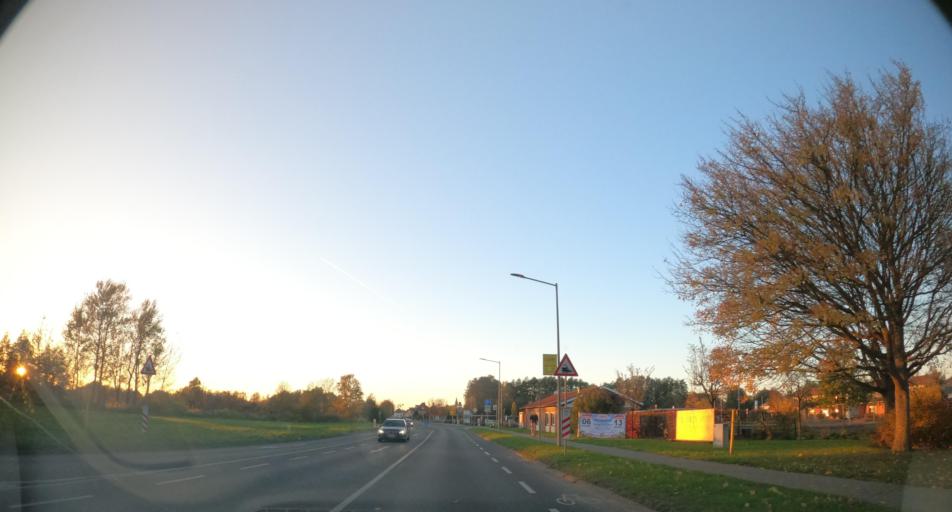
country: DE
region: Mecklenburg-Vorpommern
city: Ueckermunde
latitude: 53.7327
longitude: 14.0572
